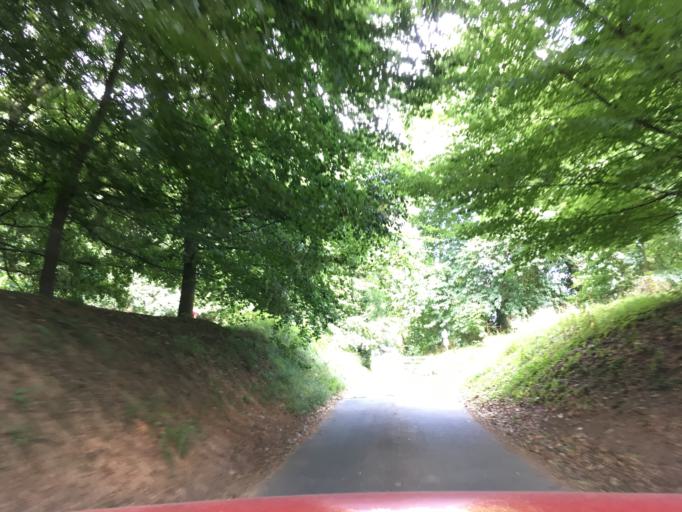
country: GB
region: England
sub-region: Kent
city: Maidstone
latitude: 51.2697
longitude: 0.5391
